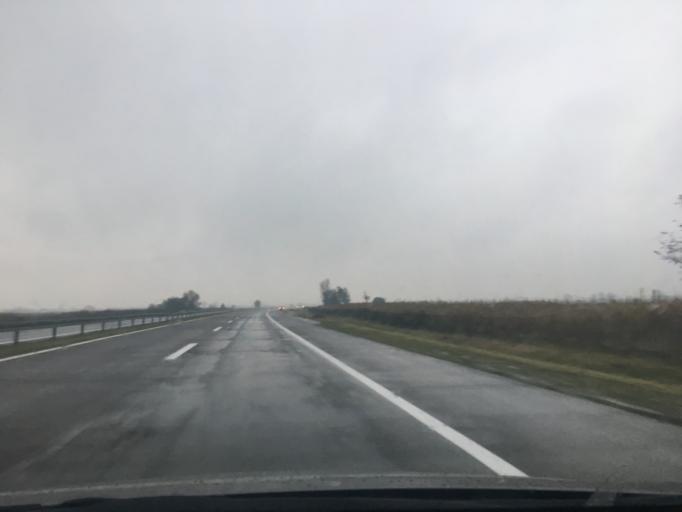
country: RS
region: Central Serbia
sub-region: Nisavski Okrug
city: Doljevac
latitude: 43.1177
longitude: 21.9177
